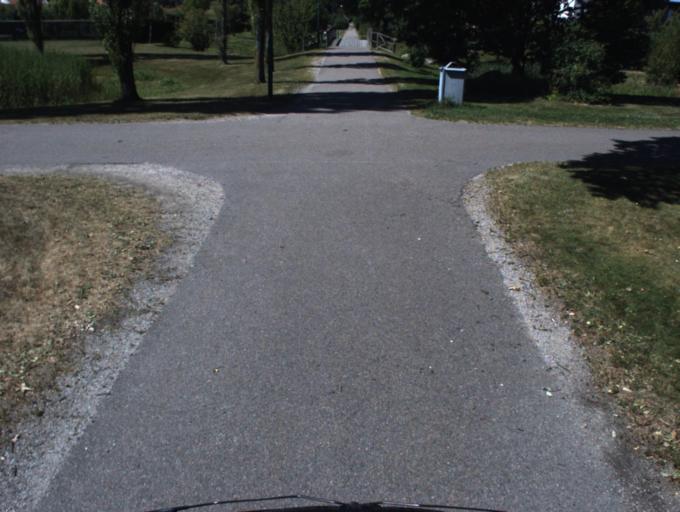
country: SE
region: Skane
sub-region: Helsingborg
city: Helsingborg
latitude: 56.0856
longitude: 12.6935
